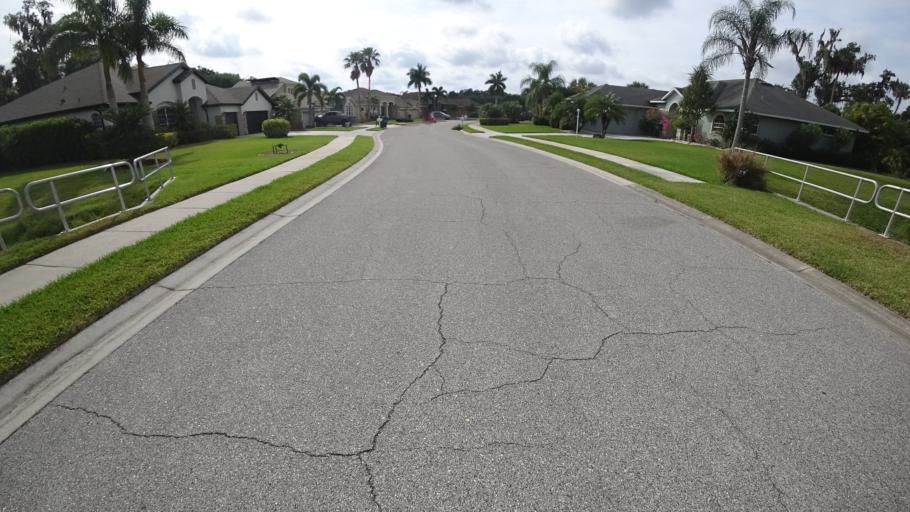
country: US
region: Florida
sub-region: Manatee County
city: Ellenton
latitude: 27.5633
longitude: -82.4700
